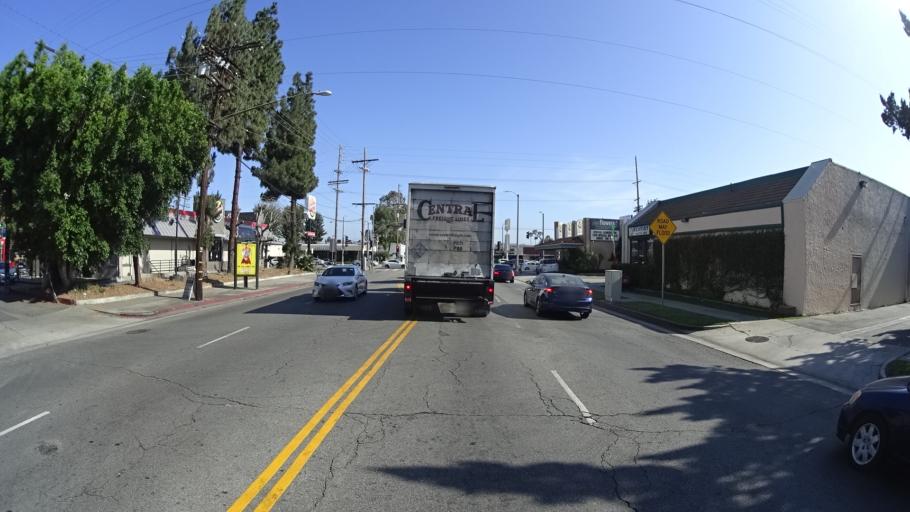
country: US
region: California
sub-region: Los Angeles County
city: Van Nuys
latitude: 34.1874
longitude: -118.4138
